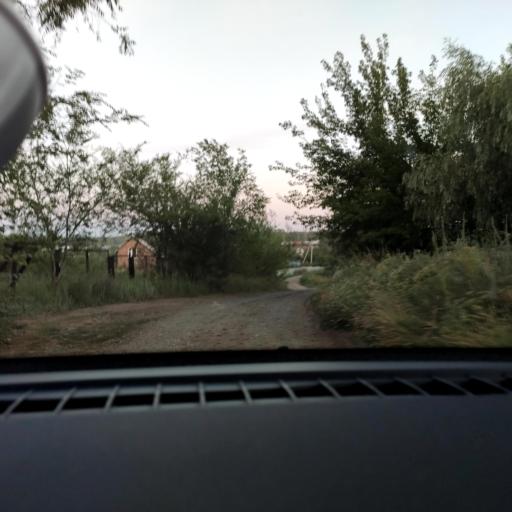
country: RU
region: Samara
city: Kinel'
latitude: 53.2530
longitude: 50.5310
